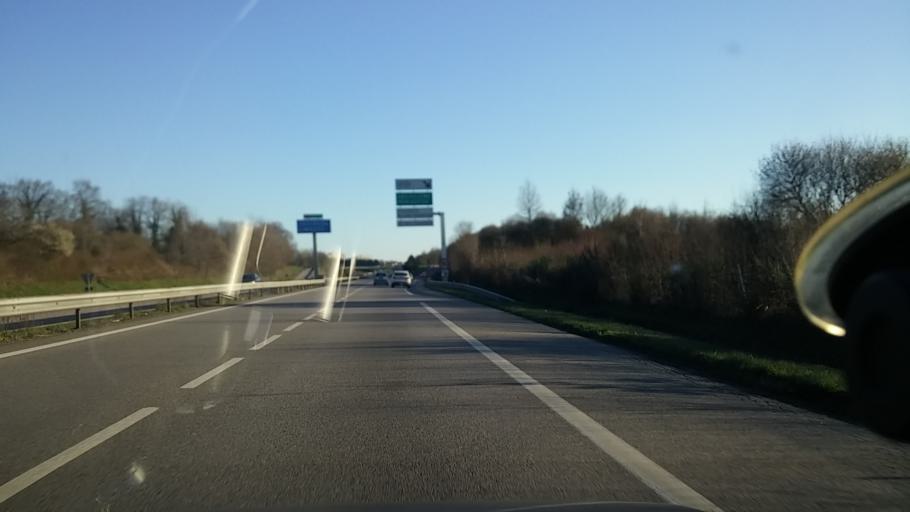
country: FR
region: Limousin
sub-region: Departement de la Haute-Vienne
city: Rilhac-Rancon
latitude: 45.8984
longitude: 1.2921
